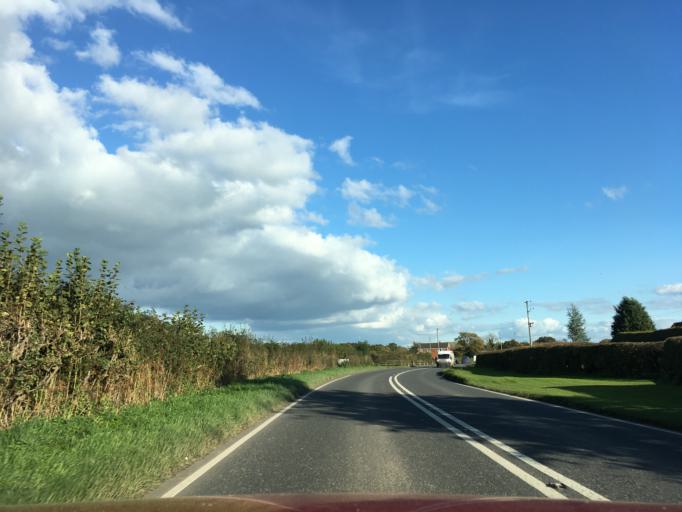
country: GB
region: England
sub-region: Herefordshire
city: Clifford
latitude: 52.1176
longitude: -3.0387
